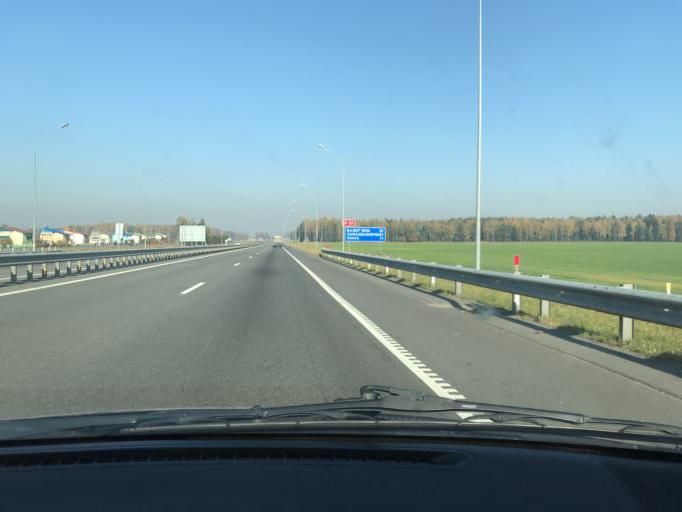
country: BY
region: Minsk
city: Slutsk
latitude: 53.2239
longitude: 27.5508
